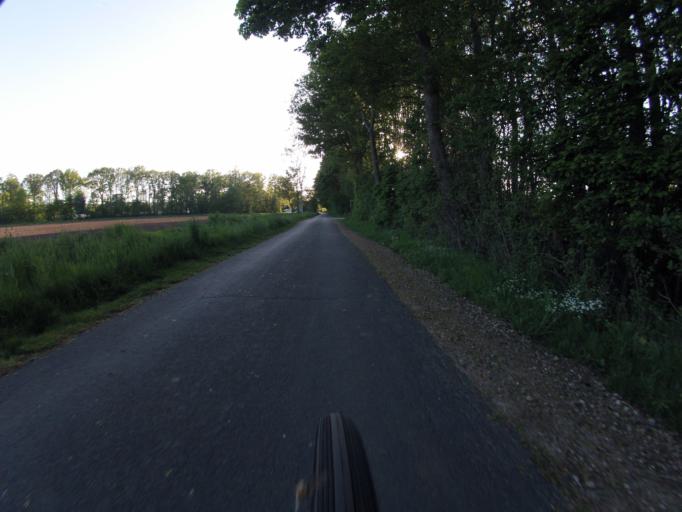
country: DE
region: North Rhine-Westphalia
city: Ibbenburen
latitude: 52.2568
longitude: 7.7544
